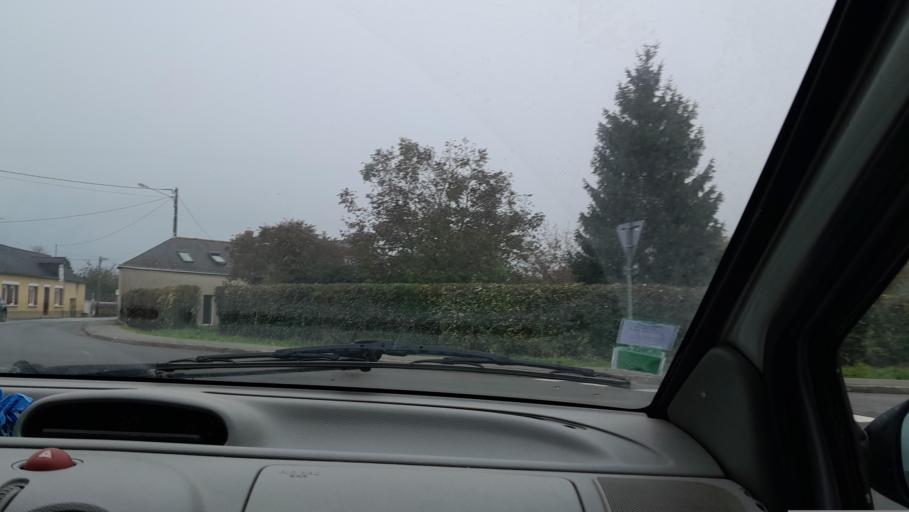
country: FR
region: Pays de la Loire
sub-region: Departement de la Mayenne
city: Saint-Berthevin
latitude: 48.0614
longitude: -0.8430
